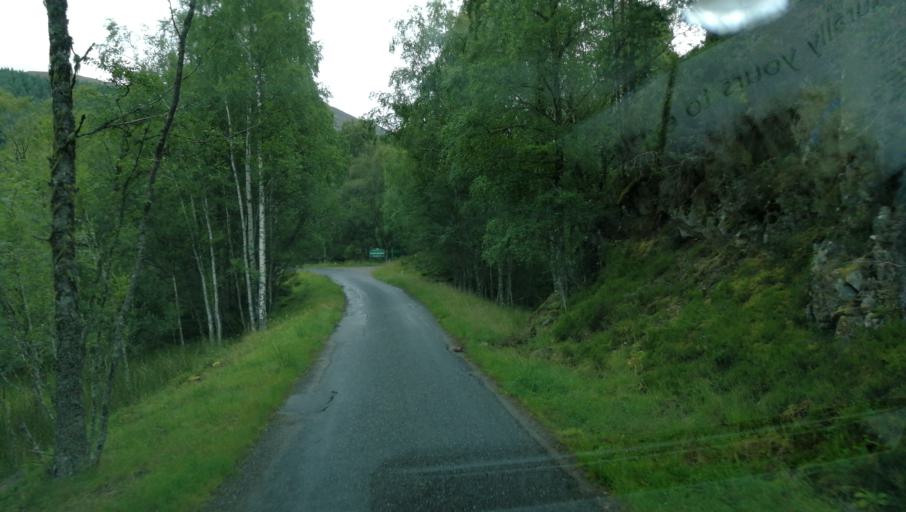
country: GB
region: Scotland
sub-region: Highland
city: Spean Bridge
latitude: 57.2915
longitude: -4.9177
